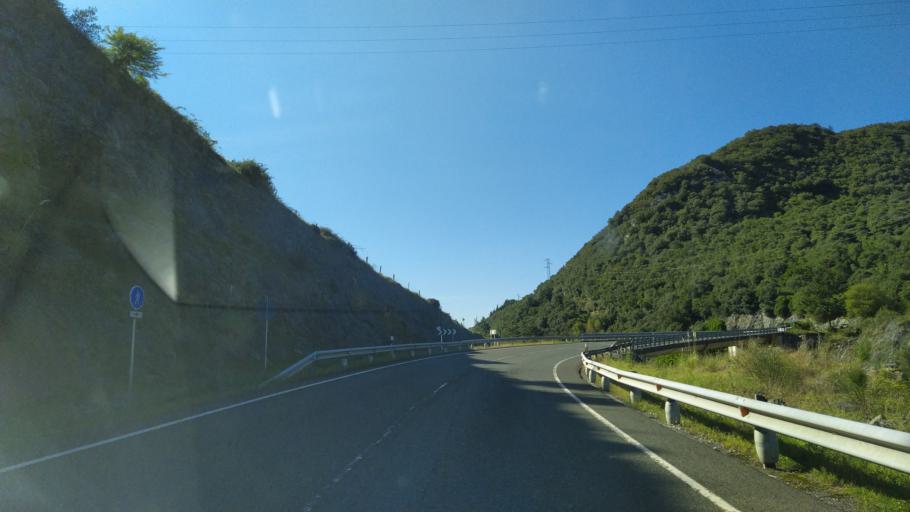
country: ES
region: Cantabria
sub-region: Provincia de Cantabria
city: Liendo
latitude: 43.3907
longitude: -3.3356
